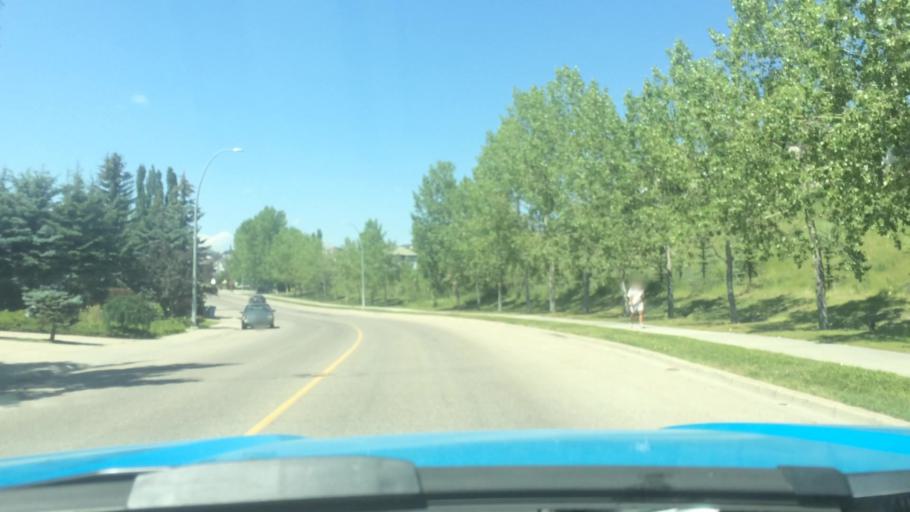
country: CA
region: Alberta
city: Calgary
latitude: 51.1345
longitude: -114.1989
